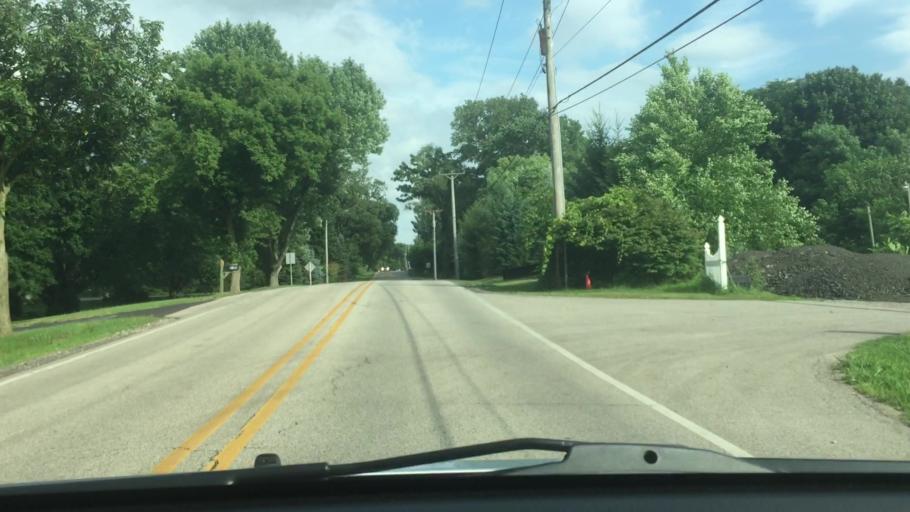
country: US
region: Illinois
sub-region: McHenry County
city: Crystal Lake
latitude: 42.2670
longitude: -88.3423
